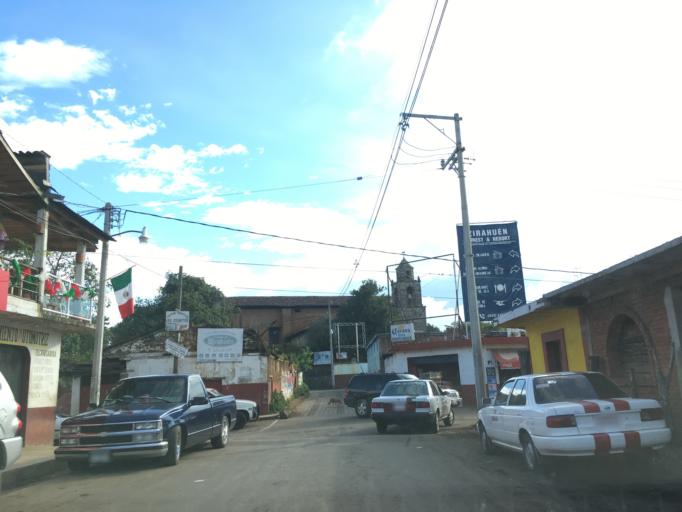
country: MX
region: Michoacan
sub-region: Patzcuaro
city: Santa Maria Huiramangaro (San Juan Tumbio)
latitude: 19.4540
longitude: -101.7306
